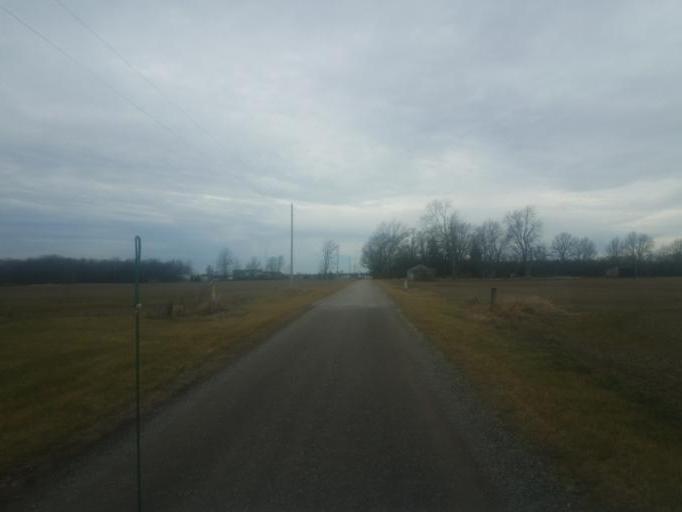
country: US
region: Ohio
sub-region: Morrow County
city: Mount Gilead
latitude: 40.6249
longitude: -82.9088
